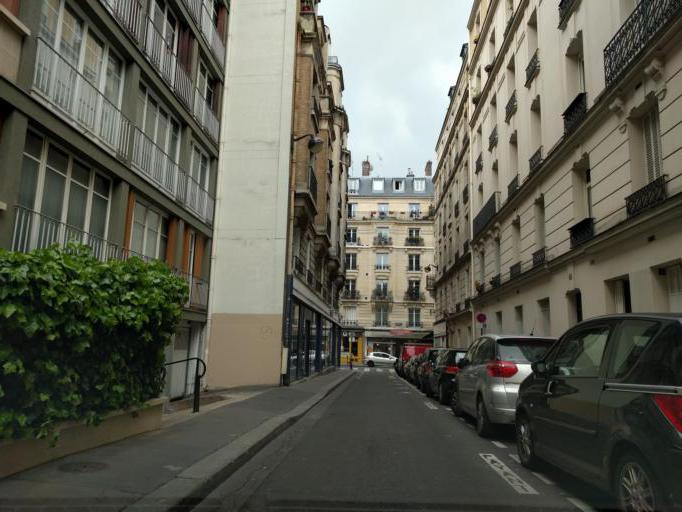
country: FR
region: Ile-de-France
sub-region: Paris
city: Paris
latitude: 48.8395
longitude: 2.3393
